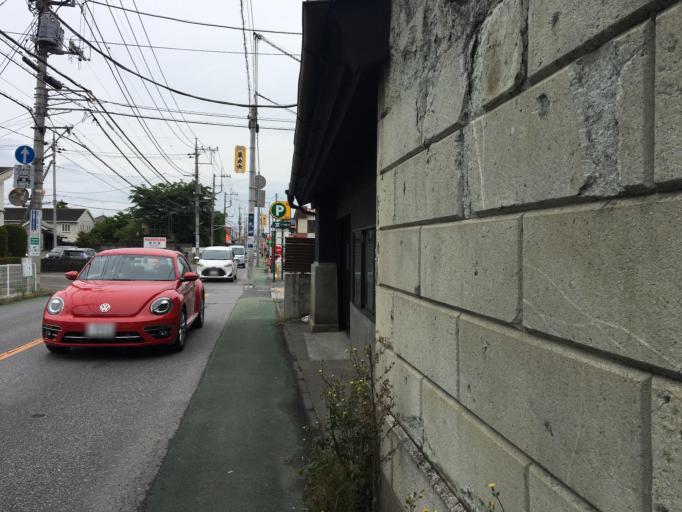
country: JP
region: Tochigi
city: Utsunomiya-shi
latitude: 36.5625
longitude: 139.8772
